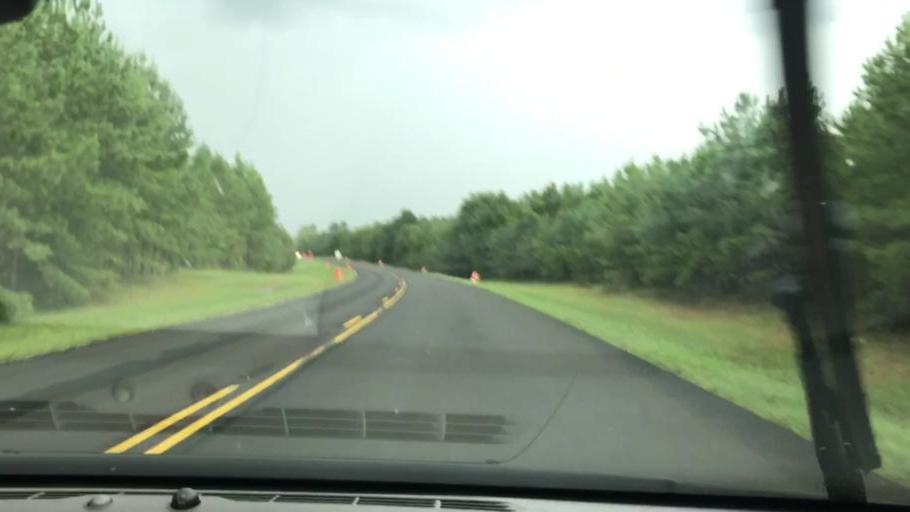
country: US
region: Georgia
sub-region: Clay County
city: Fort Gaines
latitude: 31.5099
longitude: -85.0207
